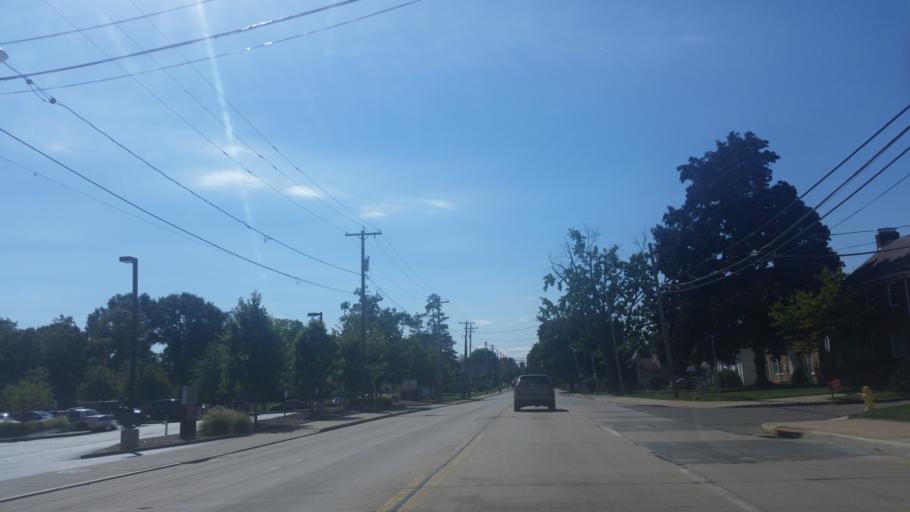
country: US
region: Ohio
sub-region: Summit County
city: Barberton
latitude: 41.0141
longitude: -81.5899
